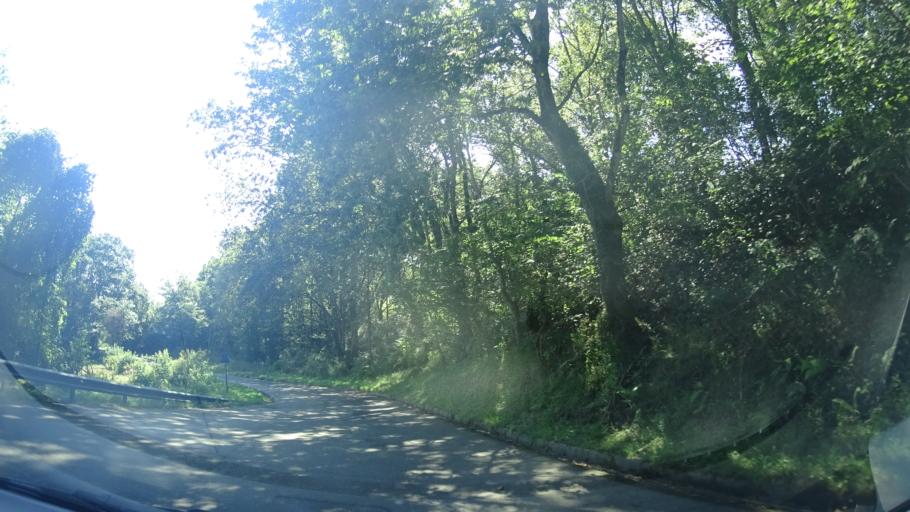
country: ES
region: Asturias
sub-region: Province of Asturias
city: Ribadesella
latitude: 43.4394
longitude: -5.0866
